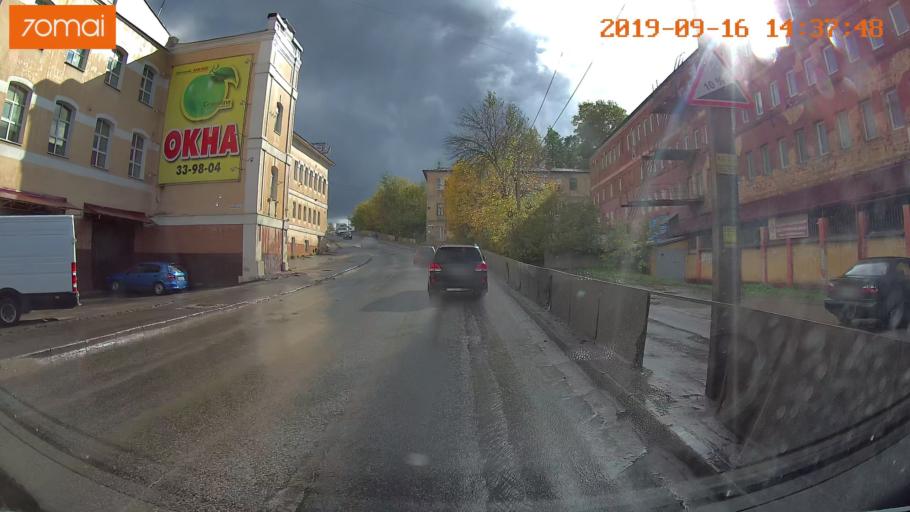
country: RU
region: Ivanovo
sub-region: Gorod Ivanovo
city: Ivanovo
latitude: 57.0121
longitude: 40.9532
